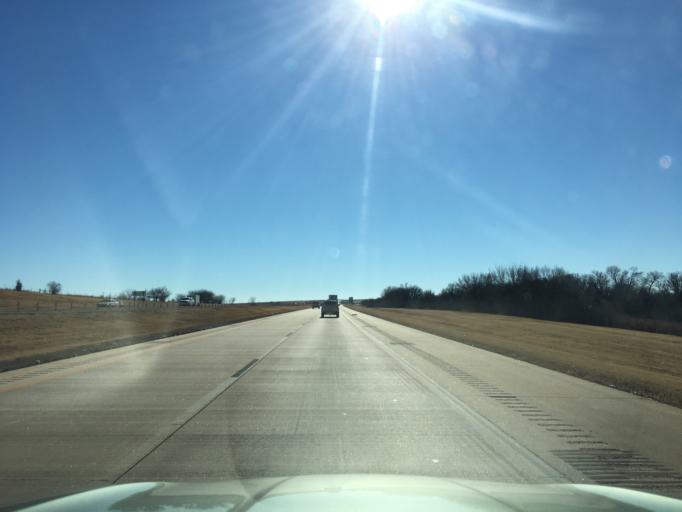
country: US
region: Oklahoma
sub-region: Noble County
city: Perry
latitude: 36.4234
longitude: -97.3272
